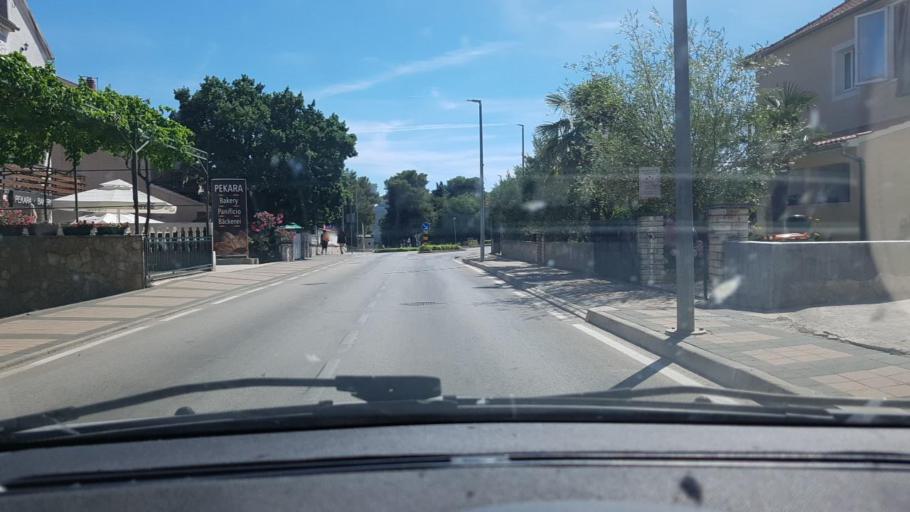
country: HR
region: Sibensko-Kniniska
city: Vodice
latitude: 43.7559
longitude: 15.7889
